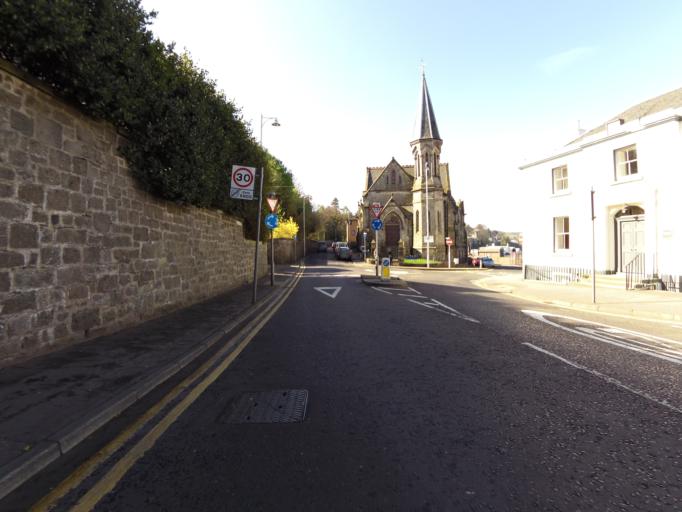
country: GB
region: Scotland
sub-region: Fife
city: Newport-On-Tay
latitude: 56.4393
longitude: -2.9420
